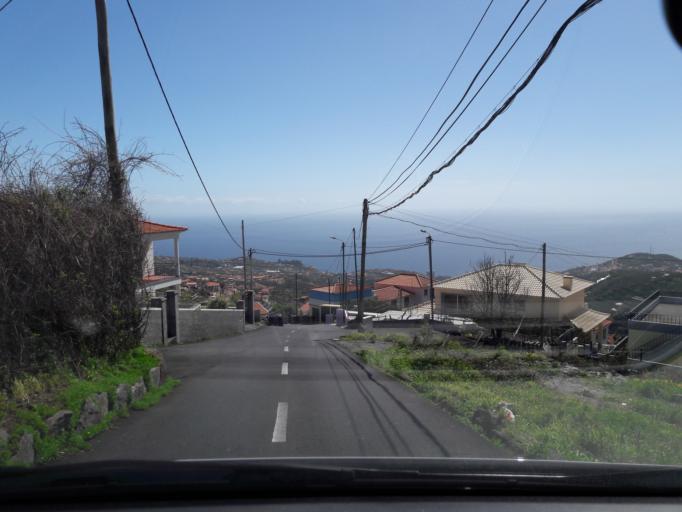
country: PT
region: Madeira
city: Camara de Lobos
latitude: 32.6710
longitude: -16.9547
